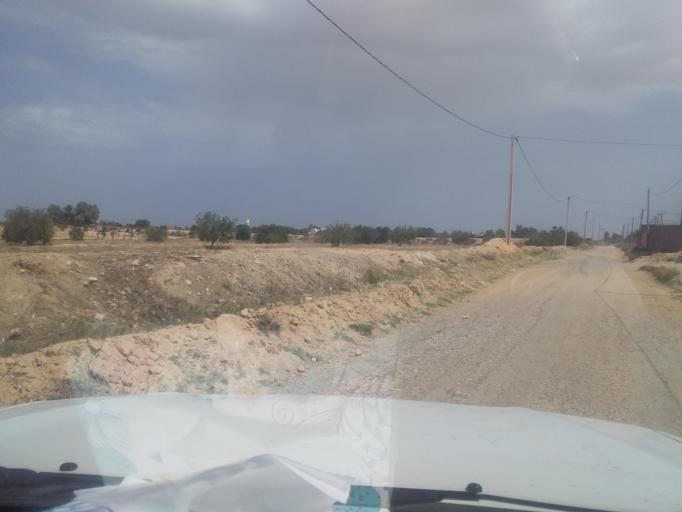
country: TN
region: Madanin
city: Medenine
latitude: 33.5840
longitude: 10.3266
